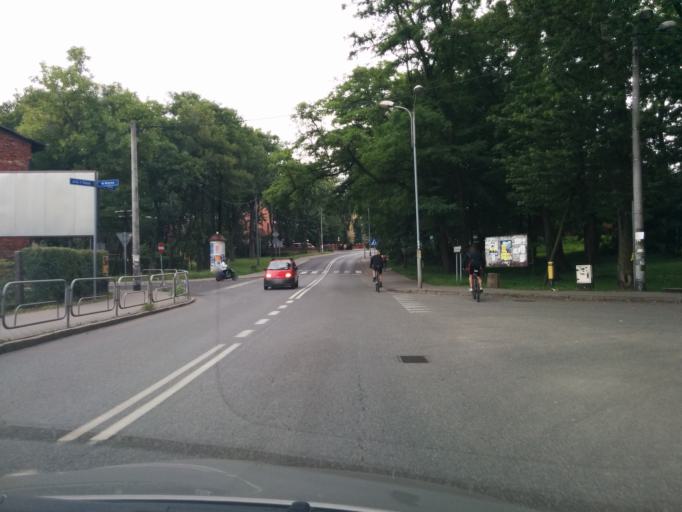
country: PL
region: Silesian Voivodeship
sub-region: Ruda Slaska
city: Ruda Slaska
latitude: 50.2693
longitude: 18.8332
